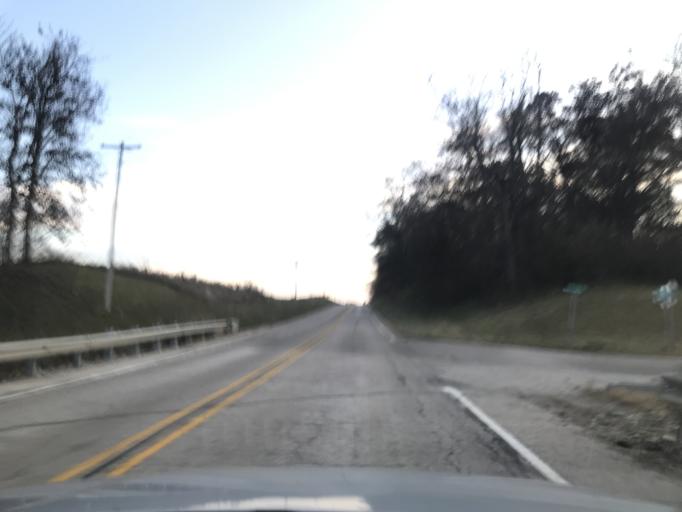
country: US
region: Illinois
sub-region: Henderson County
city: Oquawka
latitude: 40.9532
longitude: -90.8640
